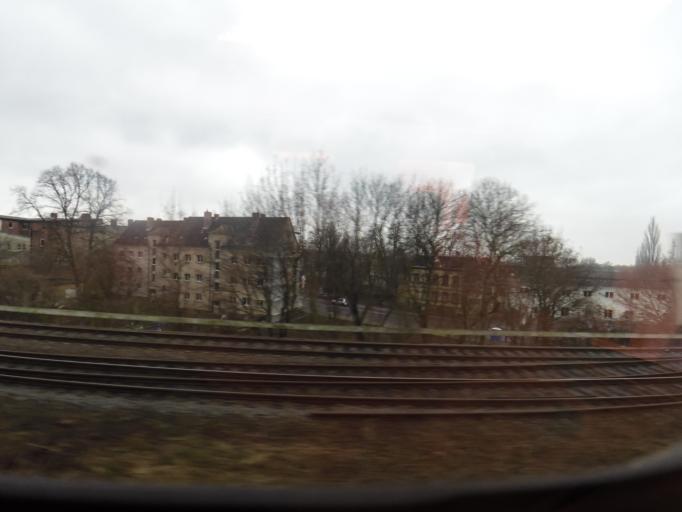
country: DE
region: Saxony-Anhalt
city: Koethen
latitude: 51.7569
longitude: 11.9871
